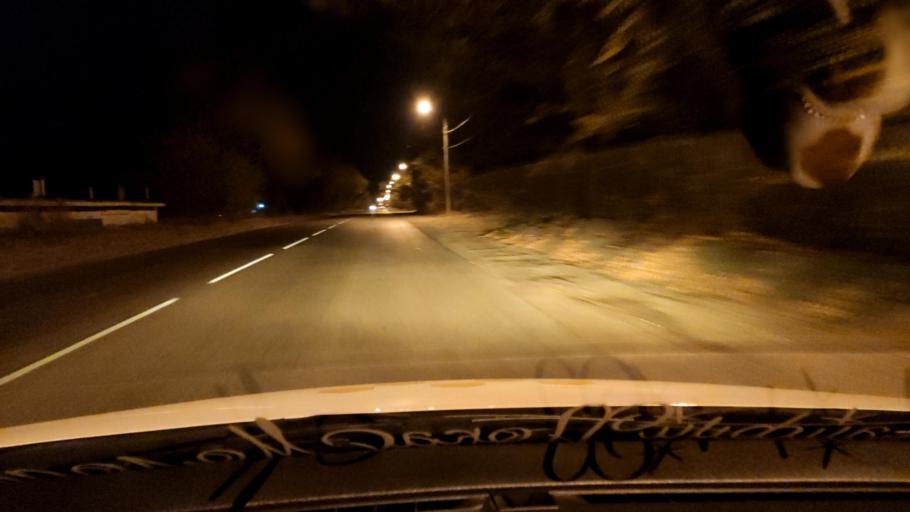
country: RU
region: Voronezj
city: Pridonskoy
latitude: 51.6836
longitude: 39.0975
